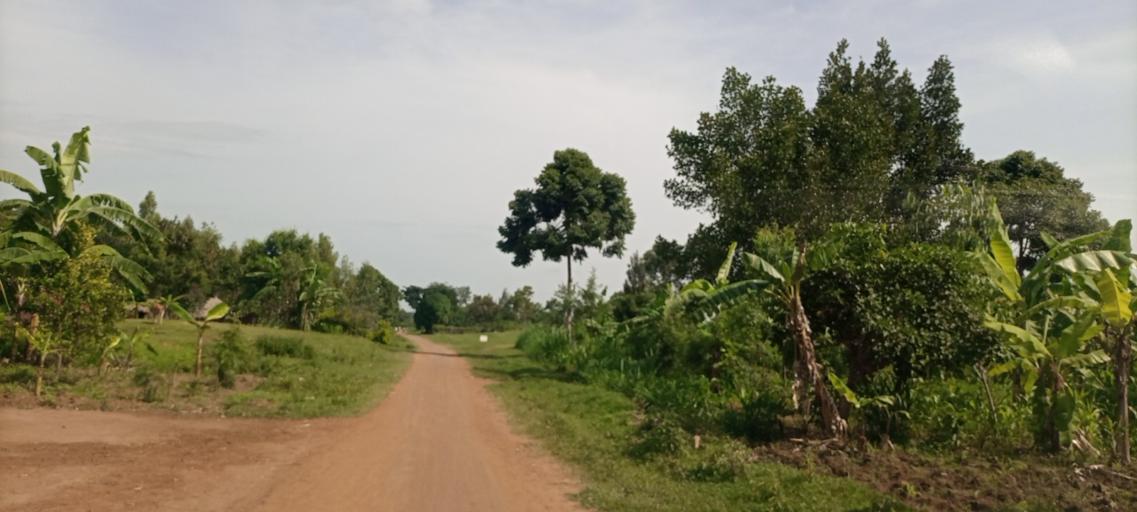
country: UG
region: Eastern Region
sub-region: Budaka District
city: Budaka
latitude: 1.1343
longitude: 34.0192
